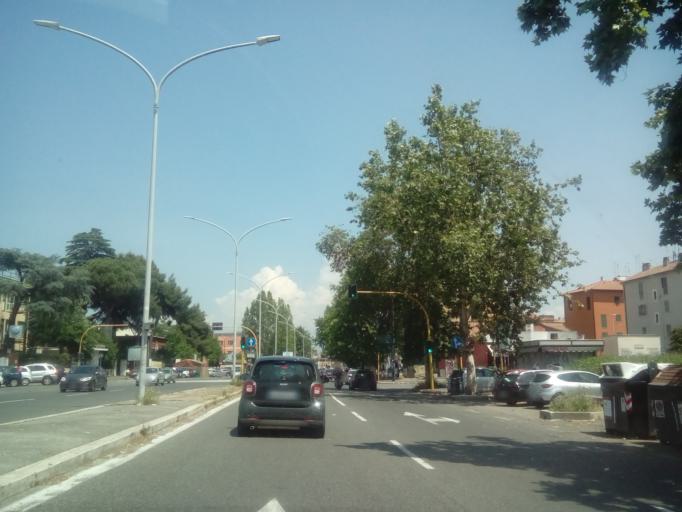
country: IT
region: Latium
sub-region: Citta metropolitana di Roma Capitale
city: Rome
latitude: 41.9103
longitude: 12.5487
